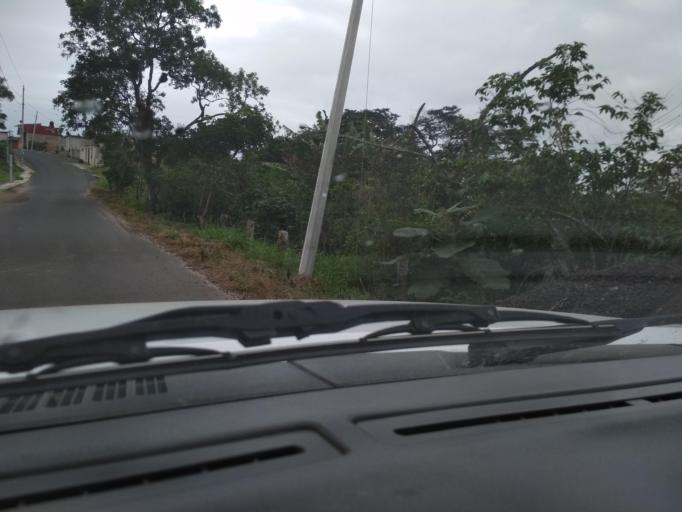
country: MX
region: Veracruz
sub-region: Emiliano Zapata
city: Dos Rios
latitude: 19.5265
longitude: -96.8018
